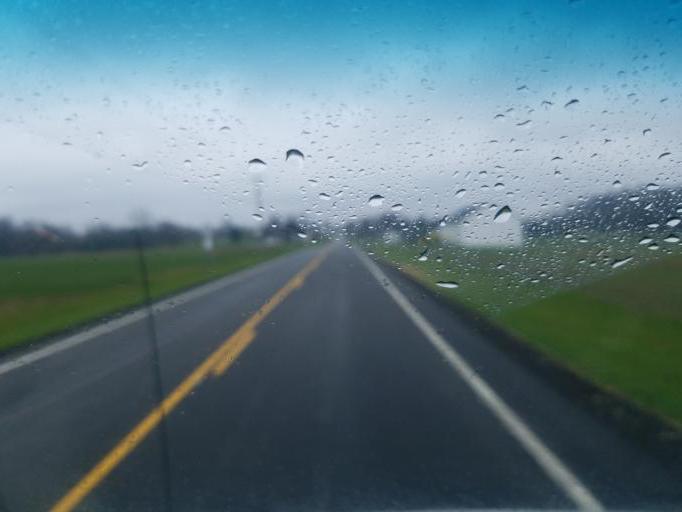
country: US
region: Ohio
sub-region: Huron County
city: Willard
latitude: 40.9650
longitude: -82.8718
